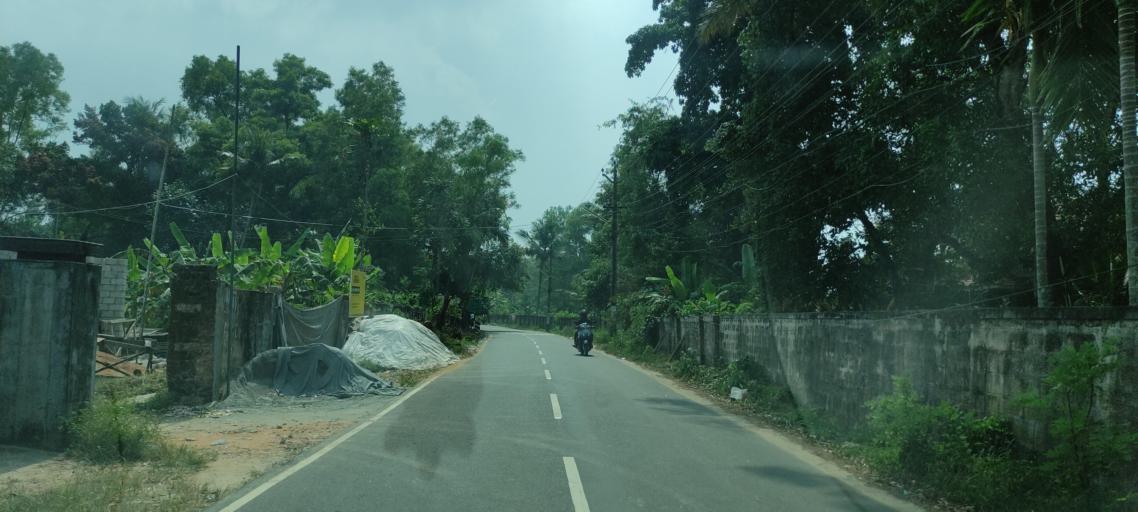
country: IN
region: Kerala
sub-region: Alappuzha
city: Alleppey
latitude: 9.5534
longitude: 76.3333
